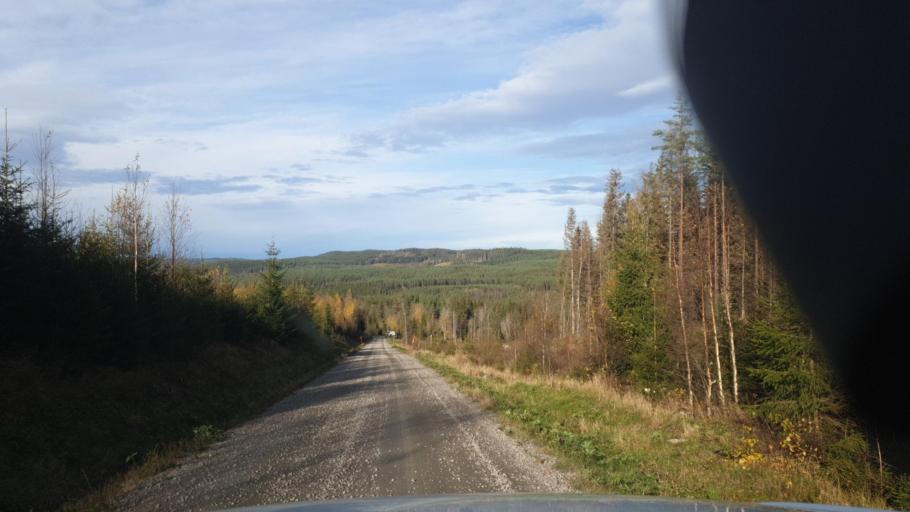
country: SE
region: Vaermland
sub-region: Eda Kommun
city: Charlottenberg
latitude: 60.0650
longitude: 12.5336
